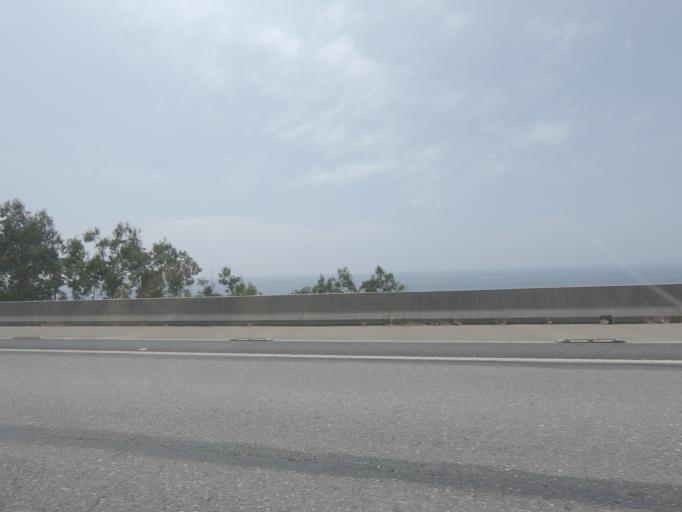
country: ES
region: Galicia
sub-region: Provincia de Pontevedra
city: A Guarda
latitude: 41.9346
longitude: -8.8838
